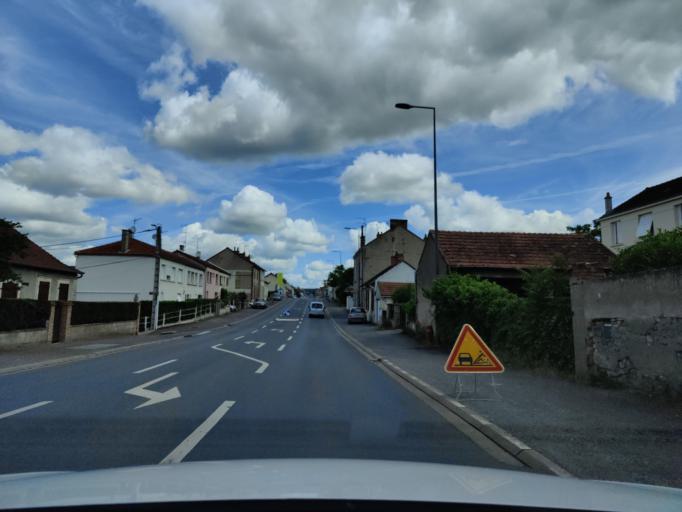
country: FR
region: Auvergne
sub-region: Departement de l'Allier
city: Desertines
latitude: 46.3503
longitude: 2.6118
